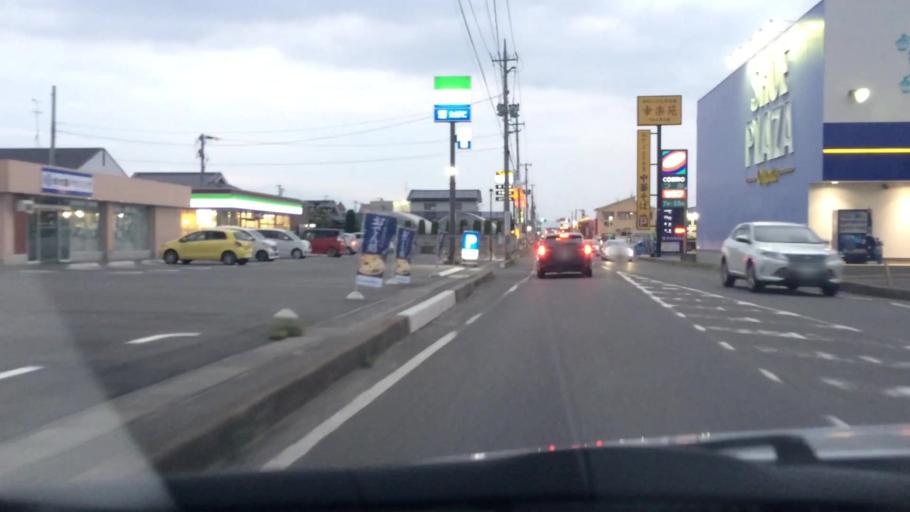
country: JP
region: Fukushima
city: Koriyama
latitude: 37.3857
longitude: 140.3322
